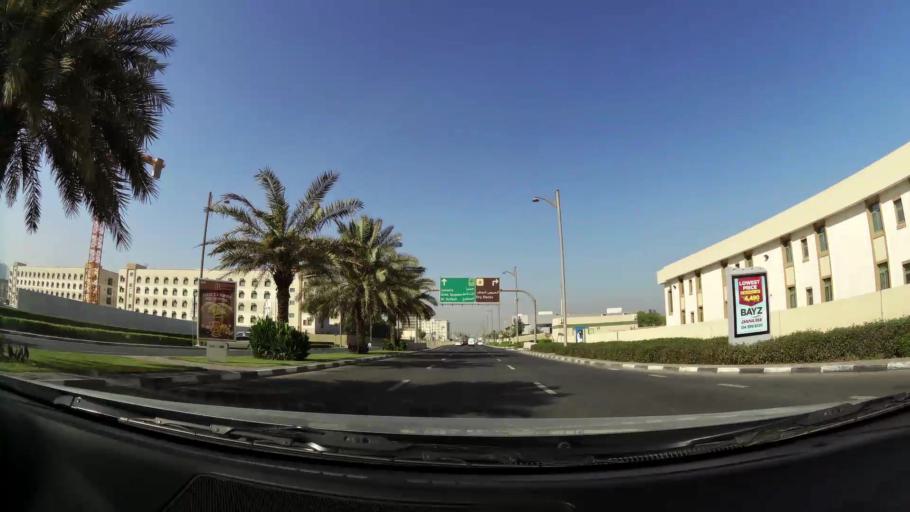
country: AE
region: Ash Shariqah
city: Sharjah
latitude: 25.2472
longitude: 55.2743
